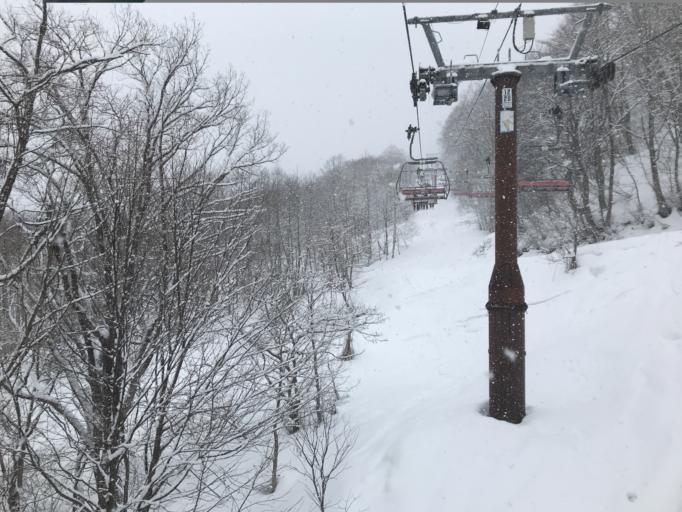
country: JP
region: Nagano
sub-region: Kitaazumi Gun
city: Hakuba
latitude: 36.7549
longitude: 137.8531
